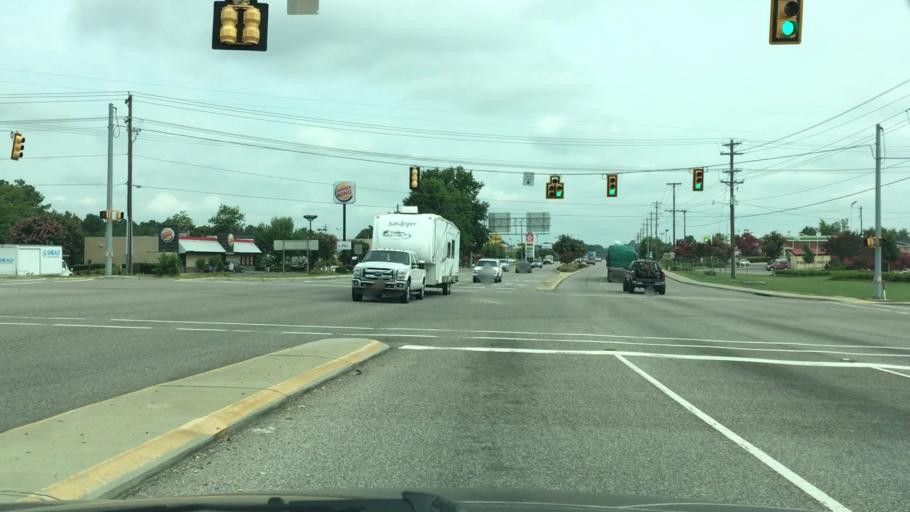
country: US
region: South Carolina
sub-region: Edgefield County
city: Murphys Estates
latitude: 33.5669
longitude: -81.9377
